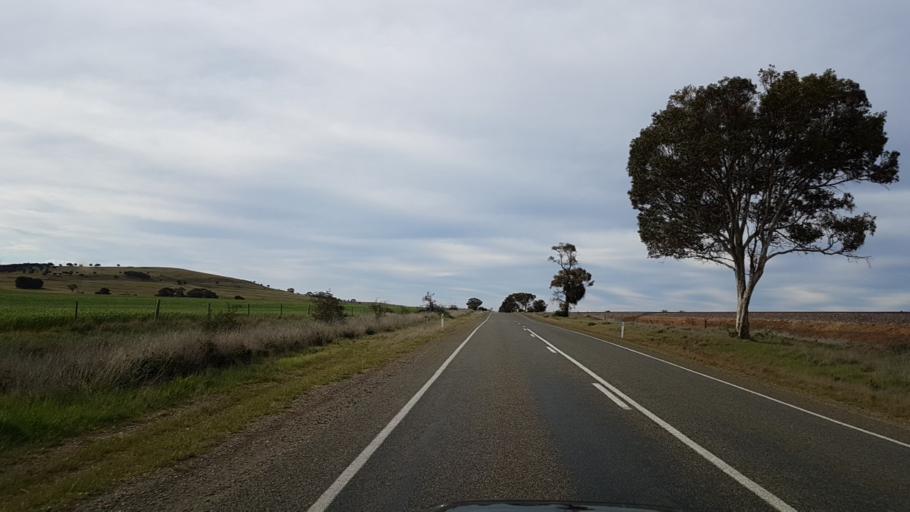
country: AU
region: South Australia
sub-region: Northern Areas
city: Jamestown
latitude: -33.1400
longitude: 138.6165
